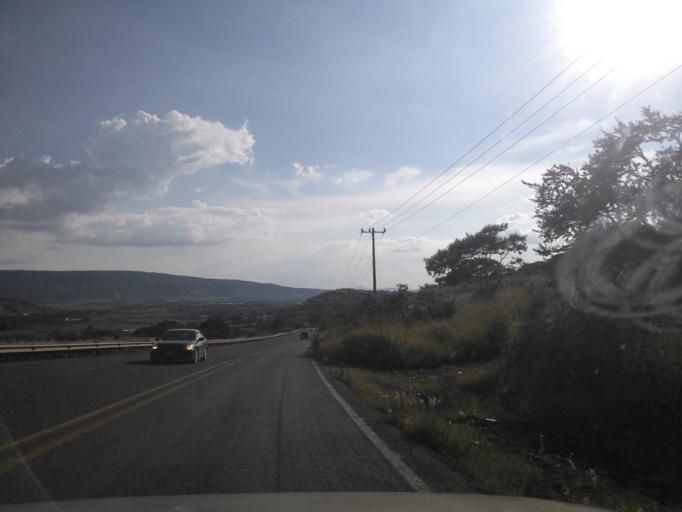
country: MX
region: Jalisco
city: Atotonilco el Alto
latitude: 20.5514
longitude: -102.5222
